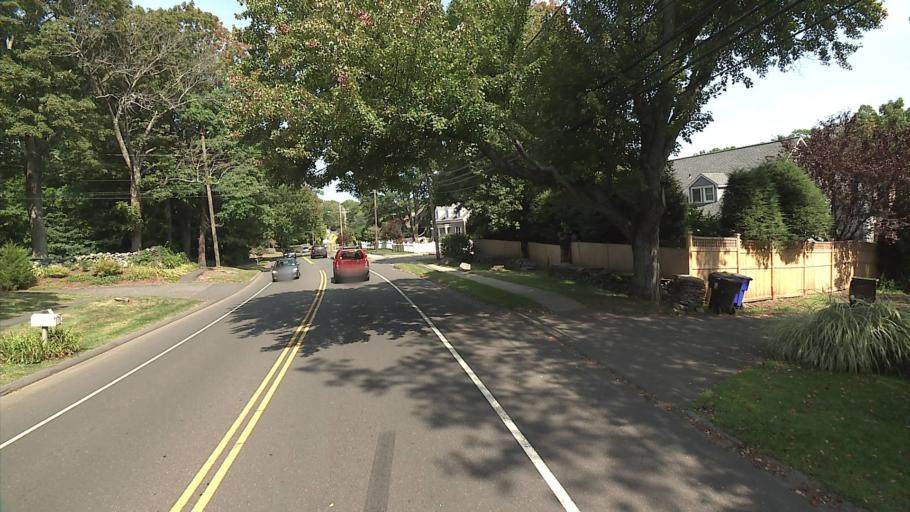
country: US
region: Connecticut
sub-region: Fairfield County
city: Fairfield
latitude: 41.1731
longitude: -73.2582
